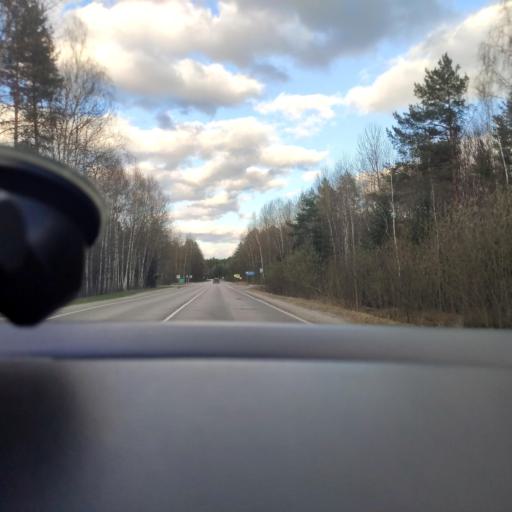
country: RU
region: Moskovskaya
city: Shaturtorf
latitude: 55.4251
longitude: 39.2970
